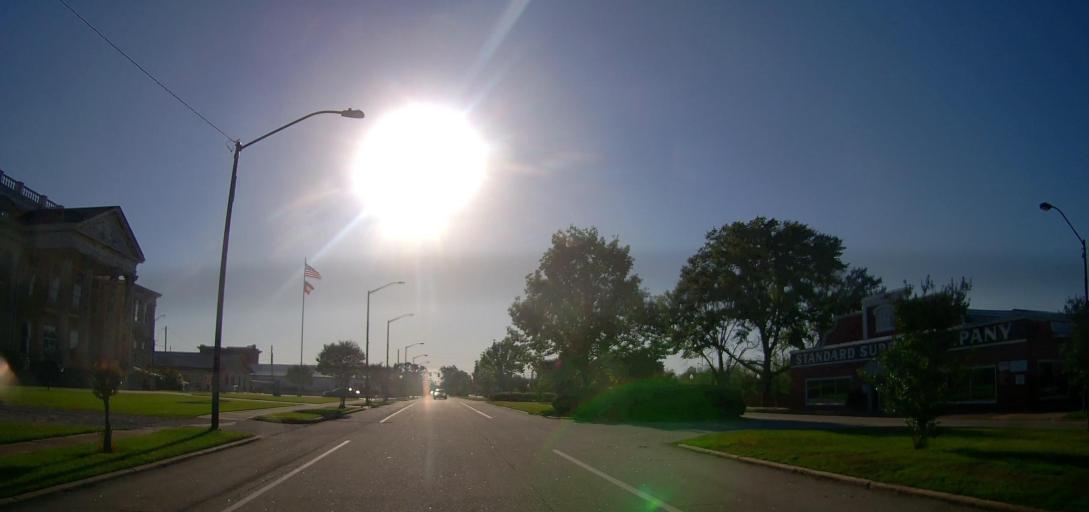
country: US
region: Georgia
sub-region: Ben Hill County
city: Fitzgerald
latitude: 31.7148
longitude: -83.2495
